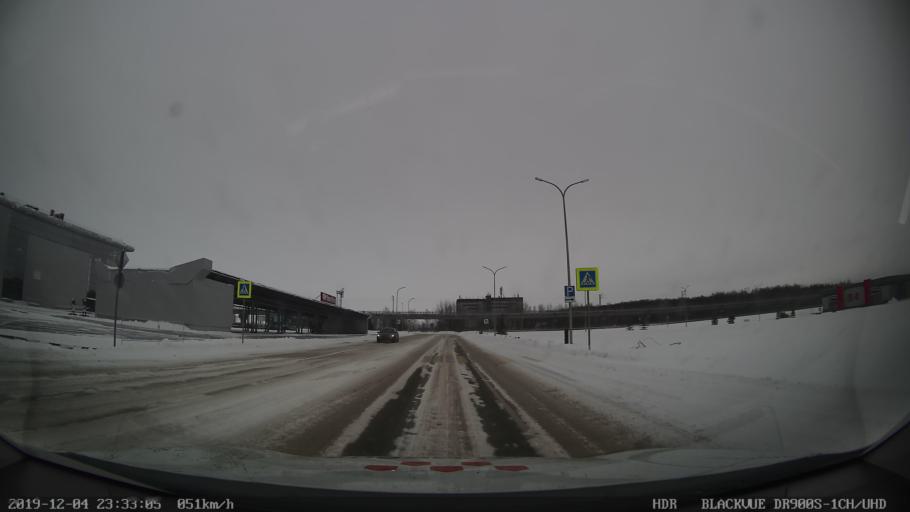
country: RU
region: Tatarstan
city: Stolbishchi
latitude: 55.6131
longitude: 49.2956
